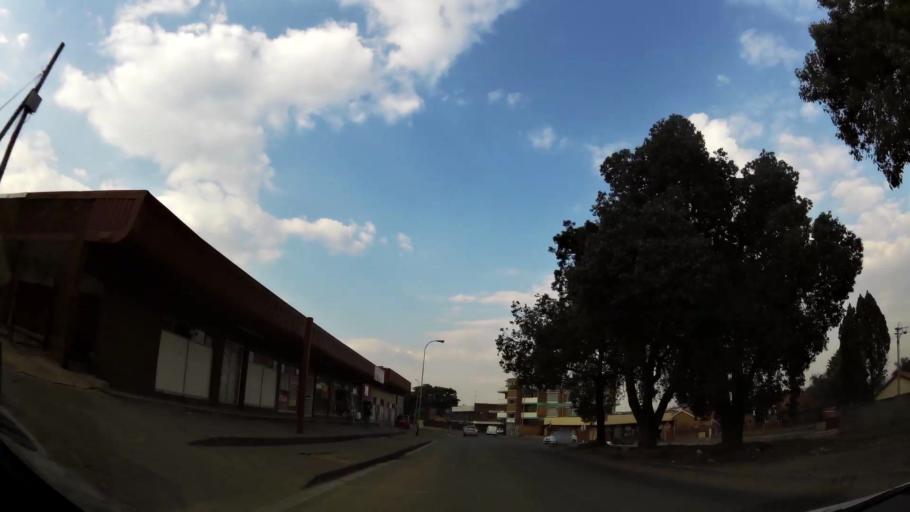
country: ZA
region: Gauteng
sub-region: Ekurhuleni Metropolitan Municipality
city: Germiston
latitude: -26.2458
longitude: 28.1990
